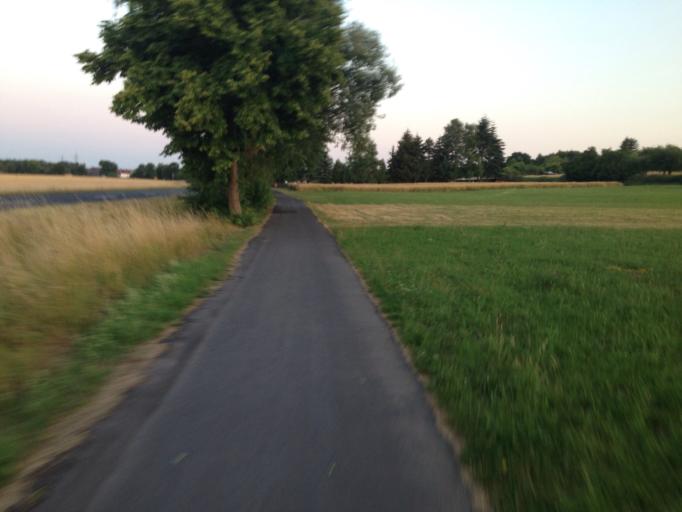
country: DE
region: Hesse
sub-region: Regierungsbezirk Giessen
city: Grossen Buseck
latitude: 50.5603
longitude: 8.7747
